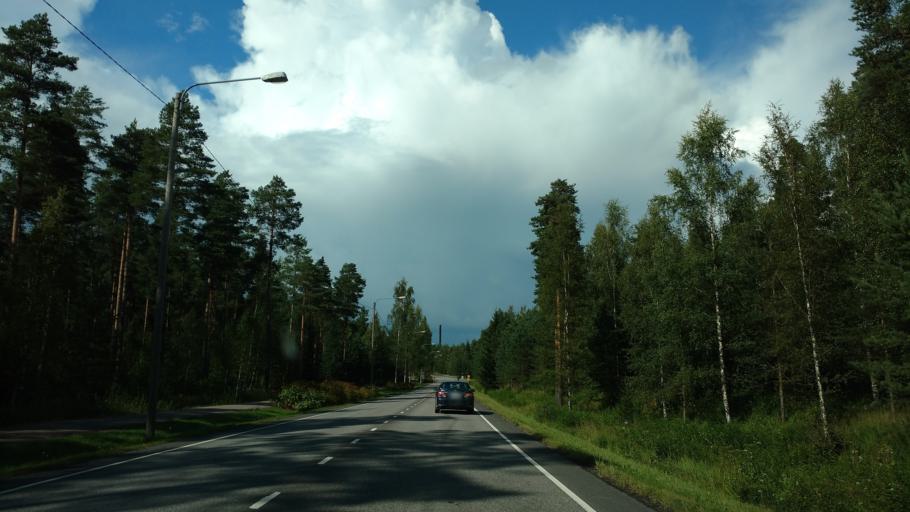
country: FI
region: Varsinais-Suomi
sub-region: Turku
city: Paimio
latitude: 60.4430
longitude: 22.7086
